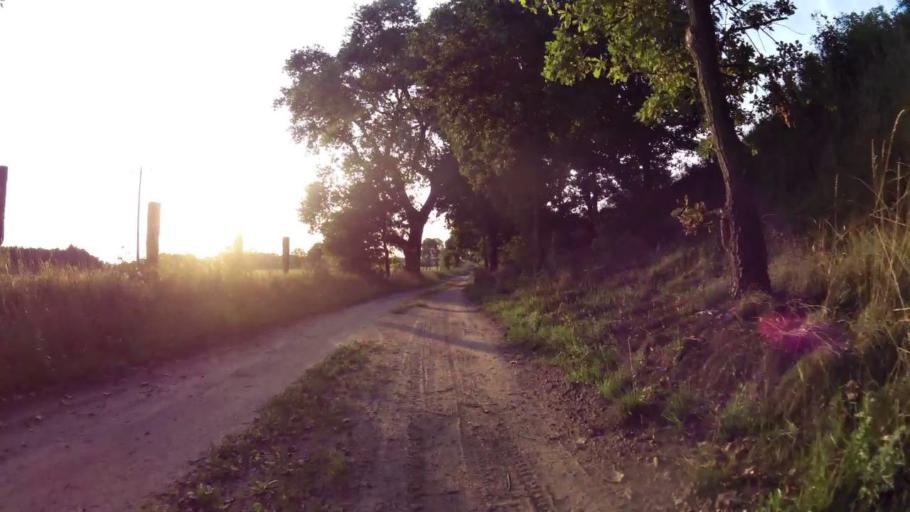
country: PL
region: West Pomeranian Voivodeship
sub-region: Powiat drawski
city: Drawsko Pomorskie
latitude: 53.4963
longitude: 15.7544
